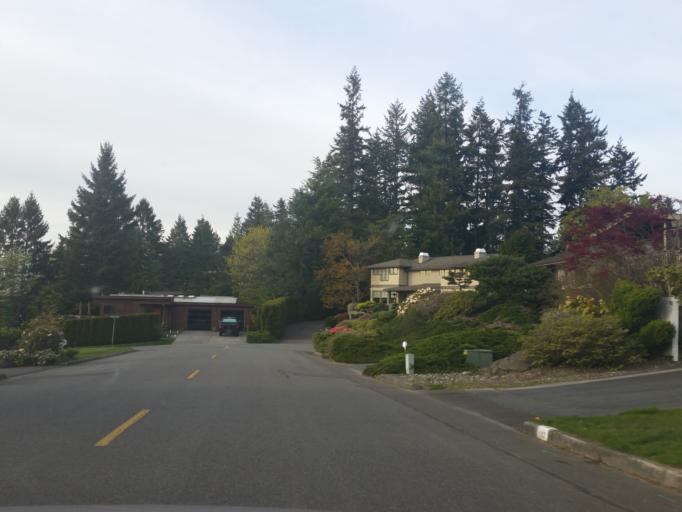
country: US
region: Washington
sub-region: Snohomish County
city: Edmonds
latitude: 47.8168
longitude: -122.3571
